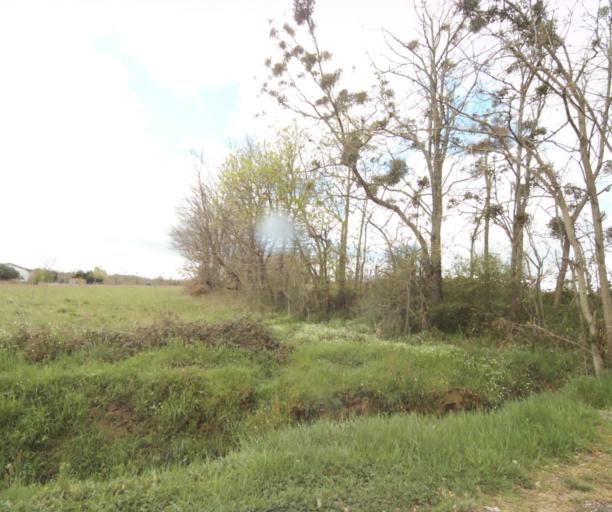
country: FR
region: Midi-Pyrenees
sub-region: Departement de l'Ariege
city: Saverdun
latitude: 43.2268
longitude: 1.5693
